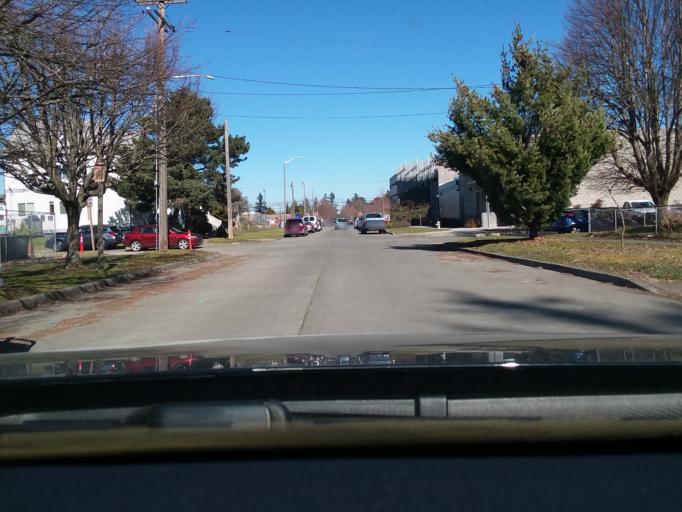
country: US
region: Washington
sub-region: Pierce County
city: Tacoma
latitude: 47.2495
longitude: -122.4526
